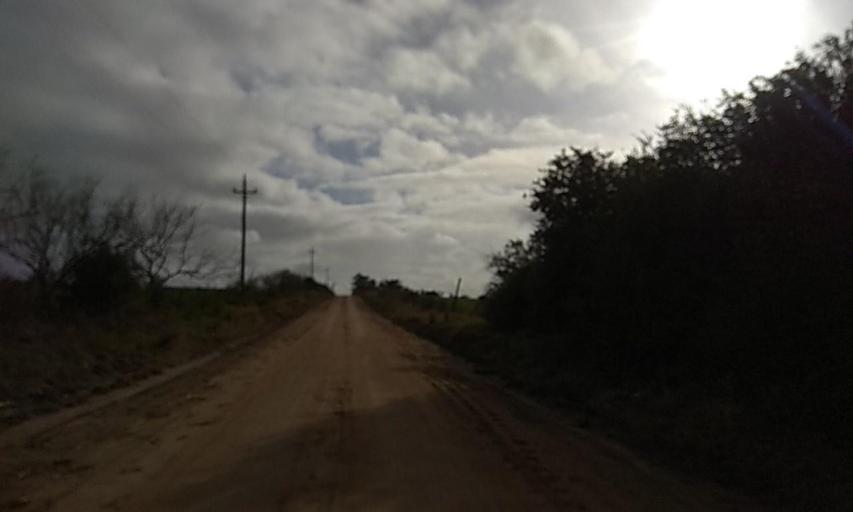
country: UY
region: Florida
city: Florida
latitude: -34.0647
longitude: -56.2304
